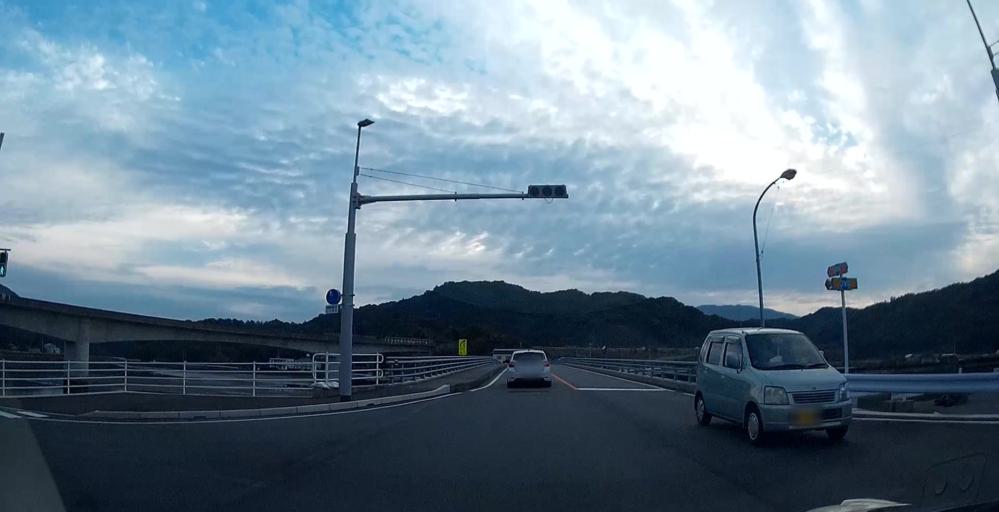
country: JP
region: Kumamoto
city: Hondo
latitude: 32.4991
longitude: 130.3950
